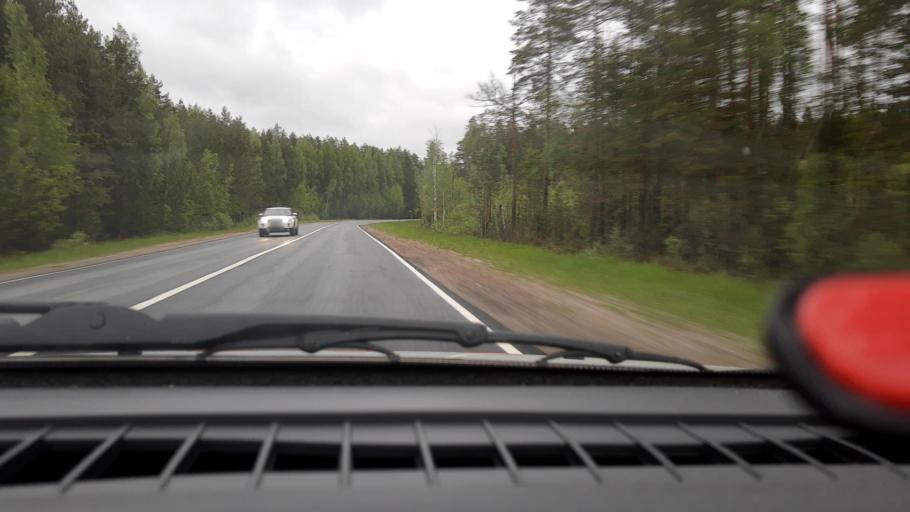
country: RU
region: Nizjnij Novgorod
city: Krasnyye Baki
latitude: 57.1754
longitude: 45.3267
